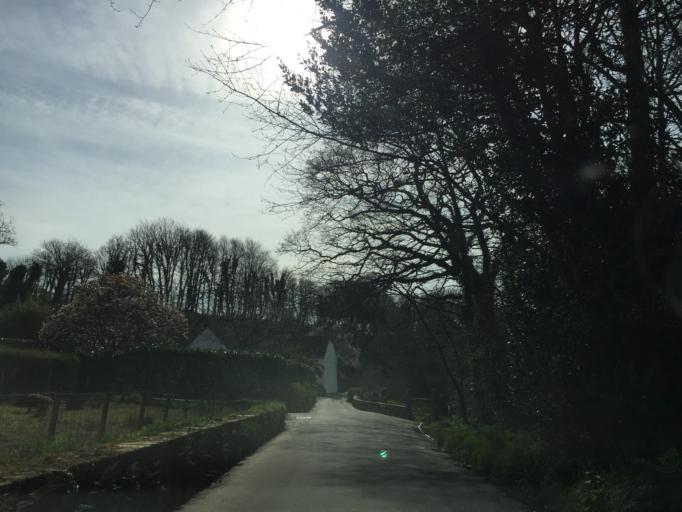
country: JE
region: St Helier
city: Saint Helier
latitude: 49.2202
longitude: -2.1466
